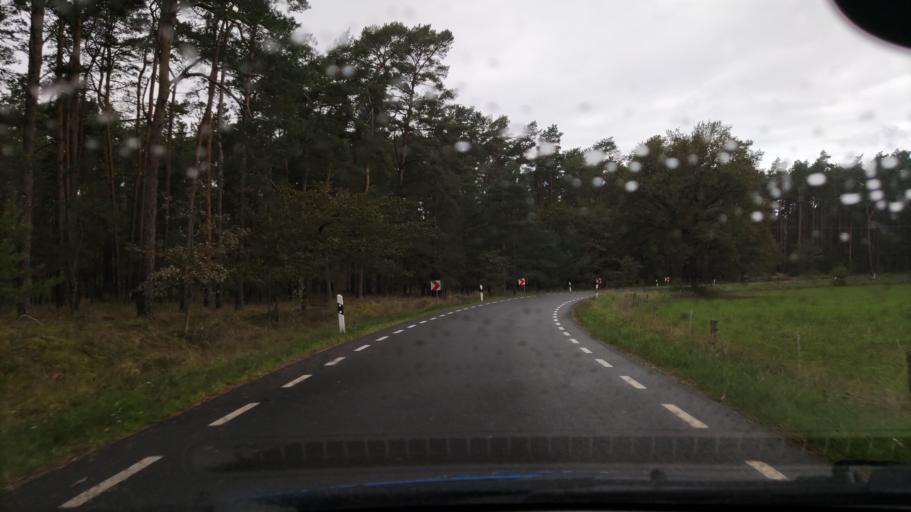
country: DE
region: Lower Saxony
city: Gartow
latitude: 52.9787
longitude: 11.5452
